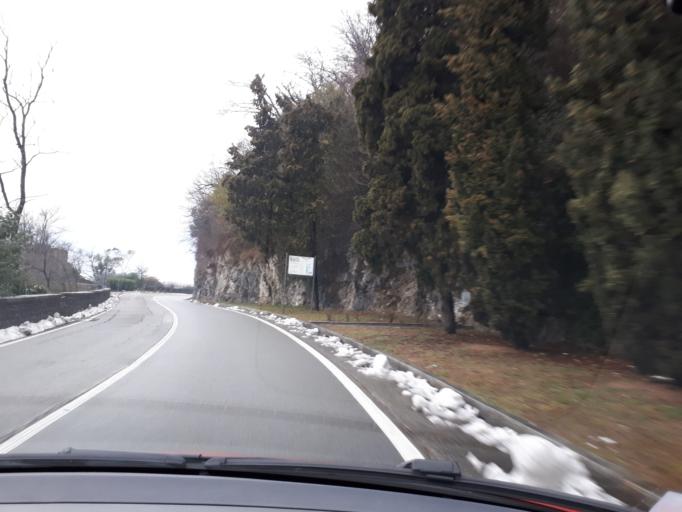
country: IT
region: Lombardy
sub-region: Provincia di Lecco
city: Varenna
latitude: 45.9861
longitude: 9.2929
